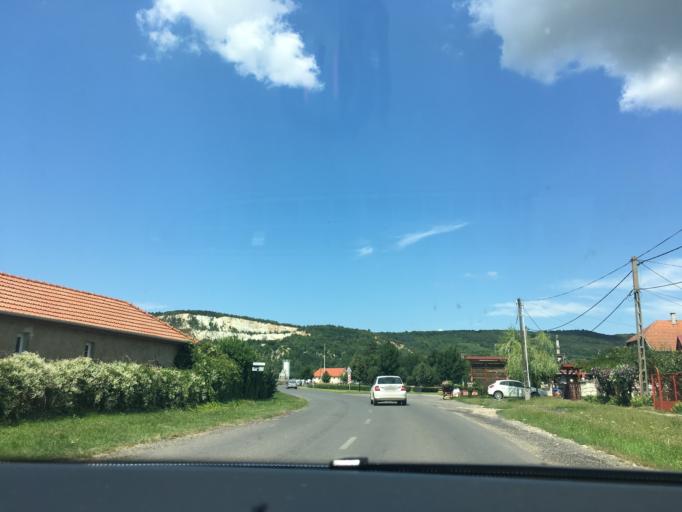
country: HU
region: Borsod-Abauj-Zemplen
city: Tarcal
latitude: 48.1724
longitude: 21.3540
